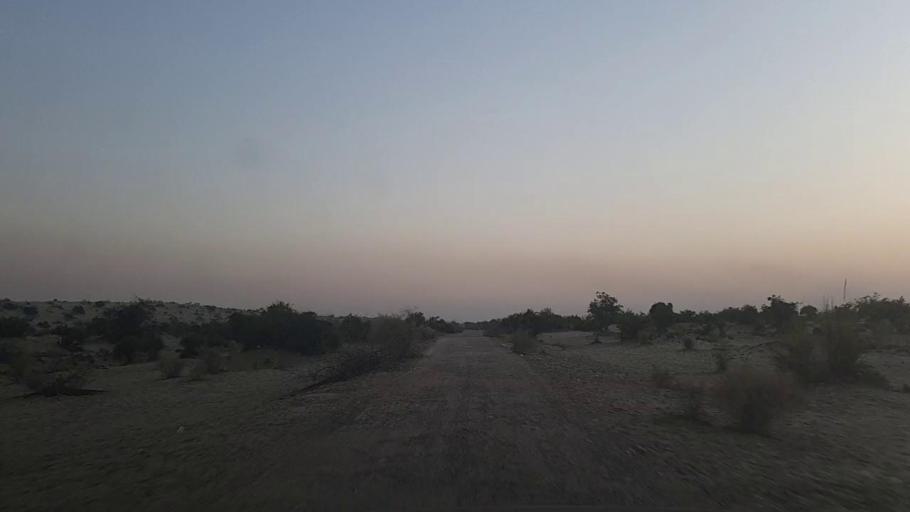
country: PK
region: Sindh
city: Jam Sahib
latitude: 26.4021
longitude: 68.8097
